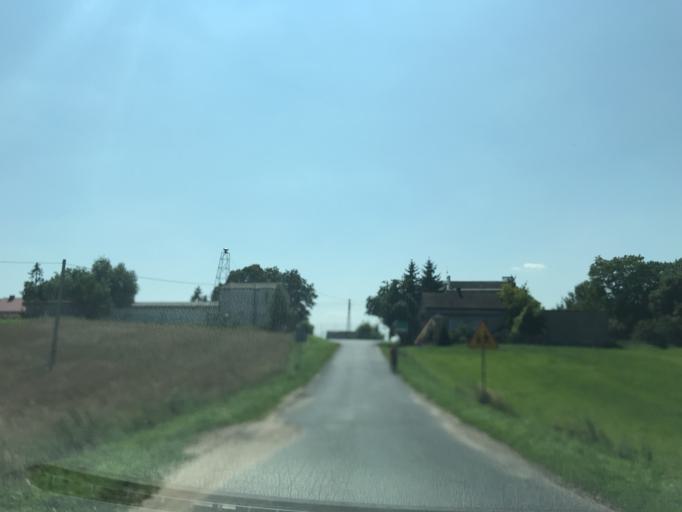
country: PL
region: Kujawsko-Pomorskie
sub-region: Powiat golubsko-dobrzynski
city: Zbojno
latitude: 52.9763
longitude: 19.1981
